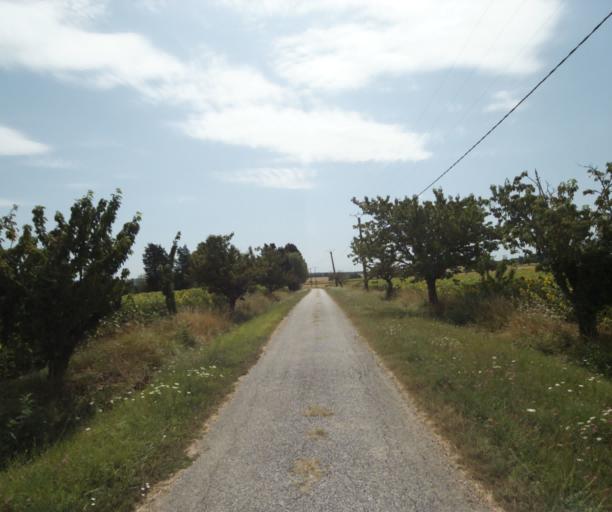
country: FR
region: Midi-Pyrenees
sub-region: Departement de la Haute-Garonne
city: Saint-Felix-Lauragais
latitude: 43.4204
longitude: 1.9129
